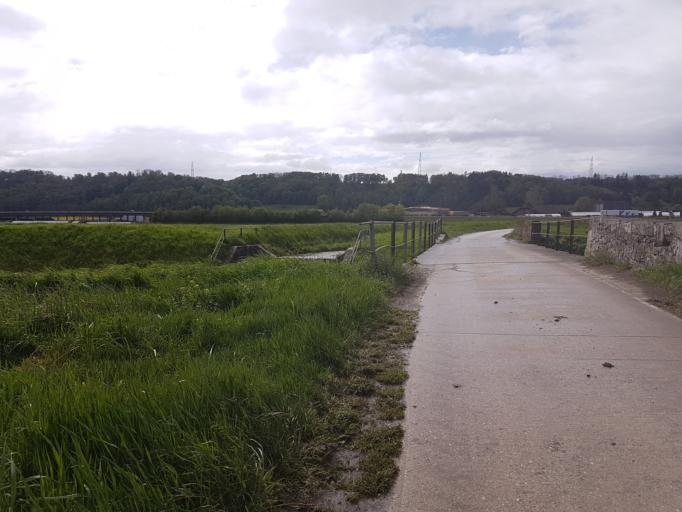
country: CH
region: Vaud
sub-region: Jura-Nord vaudois District
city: Montagny
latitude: 46.7513
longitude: 6.6064
